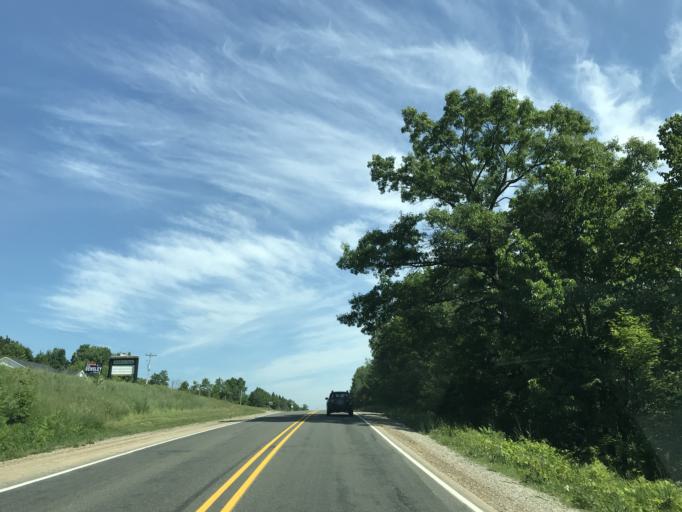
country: US
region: Michigan
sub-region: Grand Traverse County
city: Traverse City
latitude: 44.7000
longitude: -85.6255
